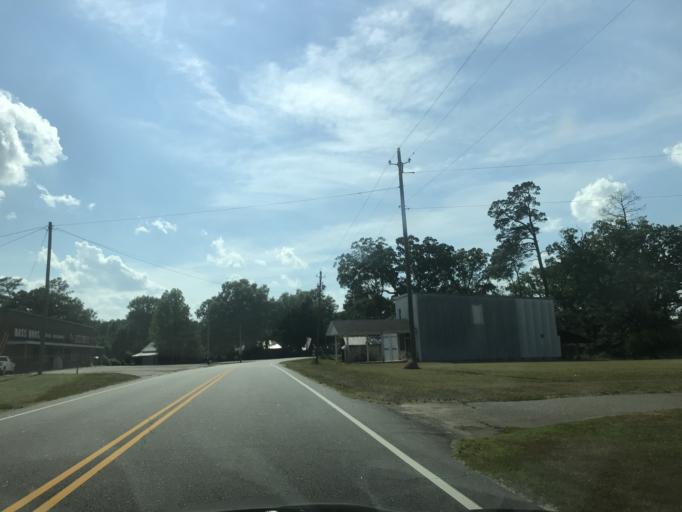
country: US
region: North Carolina
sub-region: Nash County
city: Spring Hope
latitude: 35.9612
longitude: -78.0553
